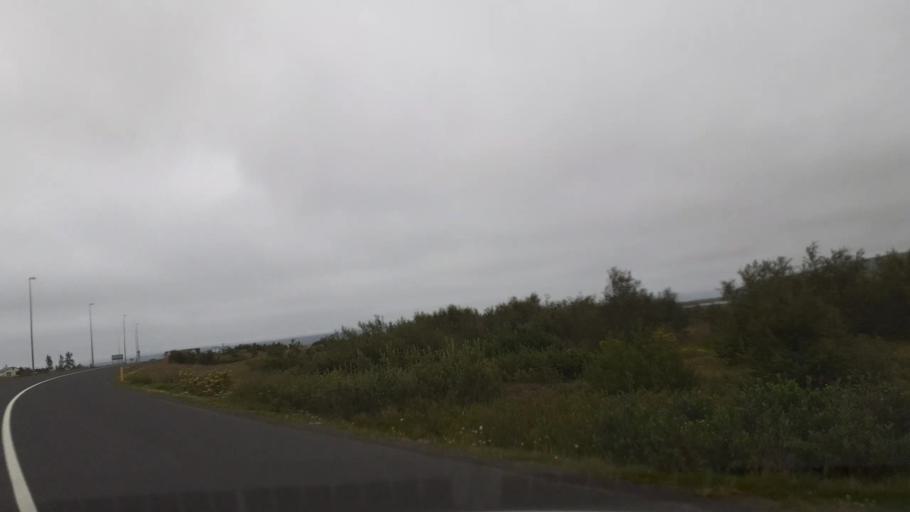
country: IS
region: Northeast
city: Dalvik
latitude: 65.9620
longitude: -18.5383
